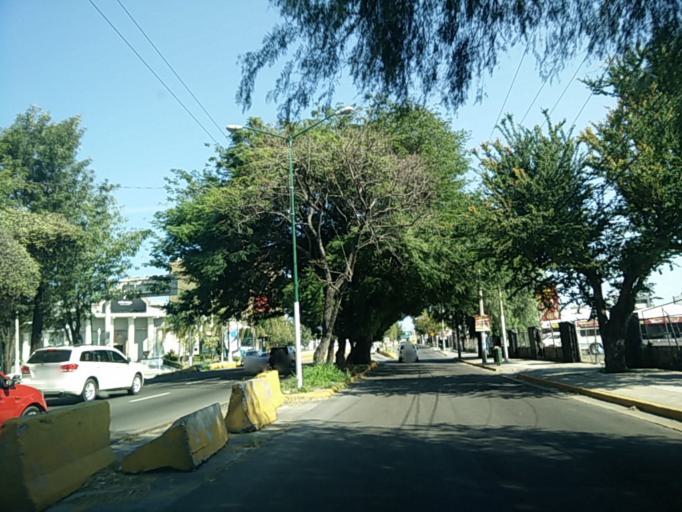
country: MX
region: Jalisco
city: Guadalajara
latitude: 20.6552
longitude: -103.4000
